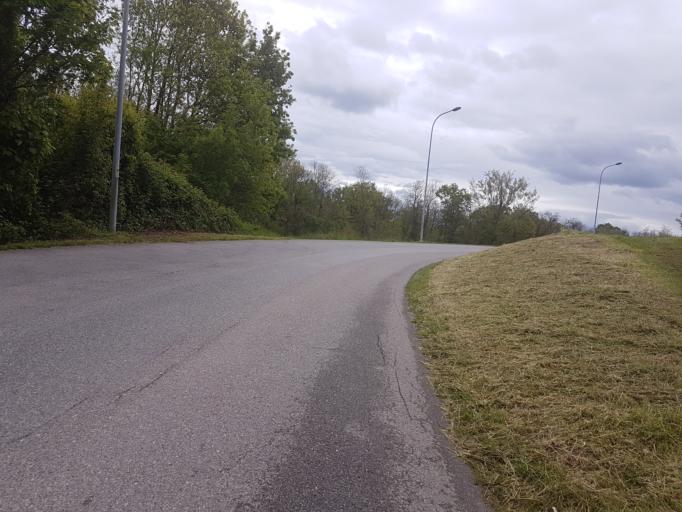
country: CH
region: Vaud
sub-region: Morges District
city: Preverenges
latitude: 46.5161
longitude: 6.5426
